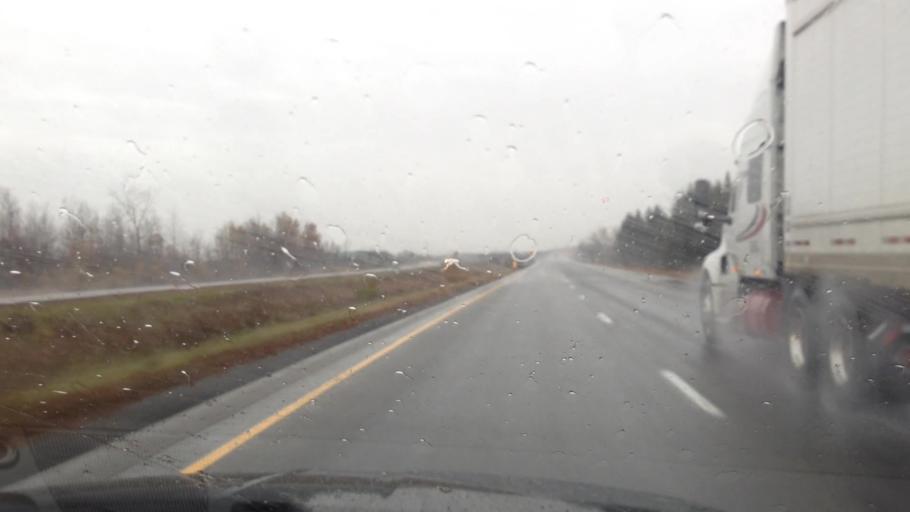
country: CA
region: Ontario
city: Casselman
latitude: 45.3129
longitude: -75.1554
